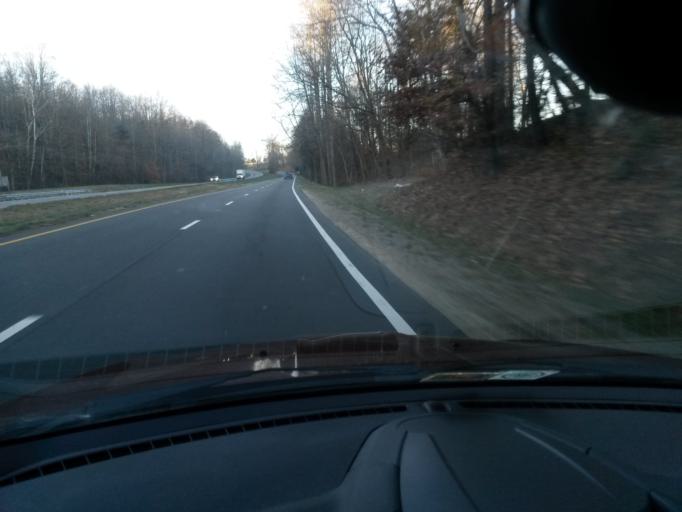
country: US
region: Virginia
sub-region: Franklin County
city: Henry Fork
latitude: 36.8615
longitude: -79.8719
